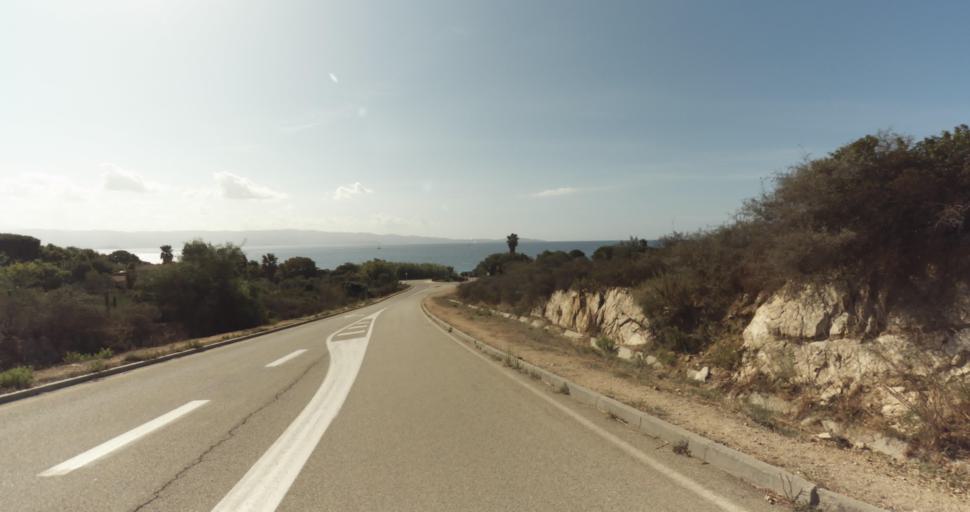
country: FR
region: Corsica
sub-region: Departement de la Corse-du-Sud
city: Ajaccio
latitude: 41.9119
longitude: 8.6439
